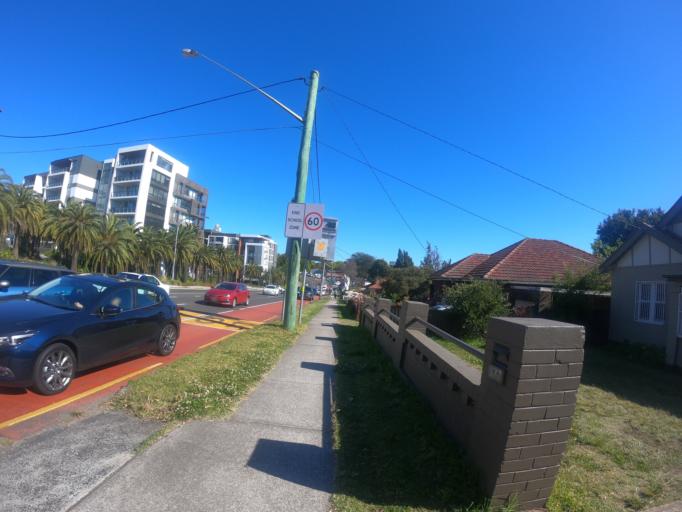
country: AU
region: New South Wales
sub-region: Ryde
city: East Ryde
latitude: -33.8177
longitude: 151.1137
